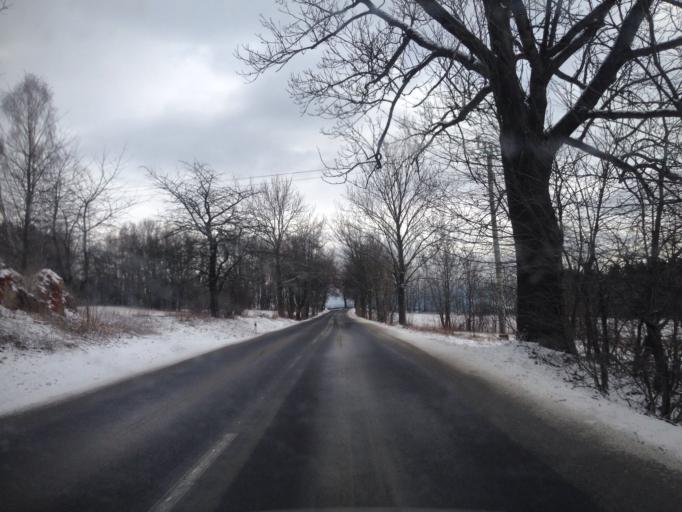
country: CZ
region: Liberecky
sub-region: Okres Semily
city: Vysoke nad Jizerou
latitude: 50.6734
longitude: 15.4097
